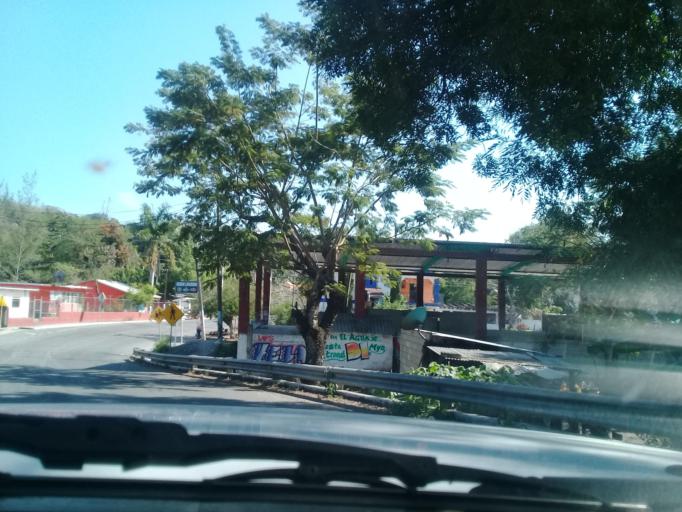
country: MX
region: Veracruz
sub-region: Emiliano Zapata
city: Plan del Rio
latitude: 19.4186
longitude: -96.6167
